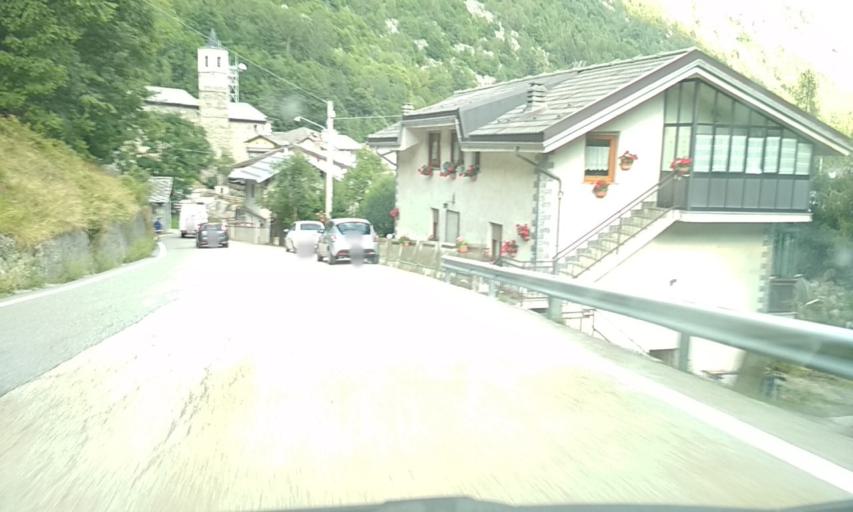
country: IT
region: Piedmont
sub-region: Provincia di Torino
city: Noasca
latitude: 45.4542
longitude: 7.3115
